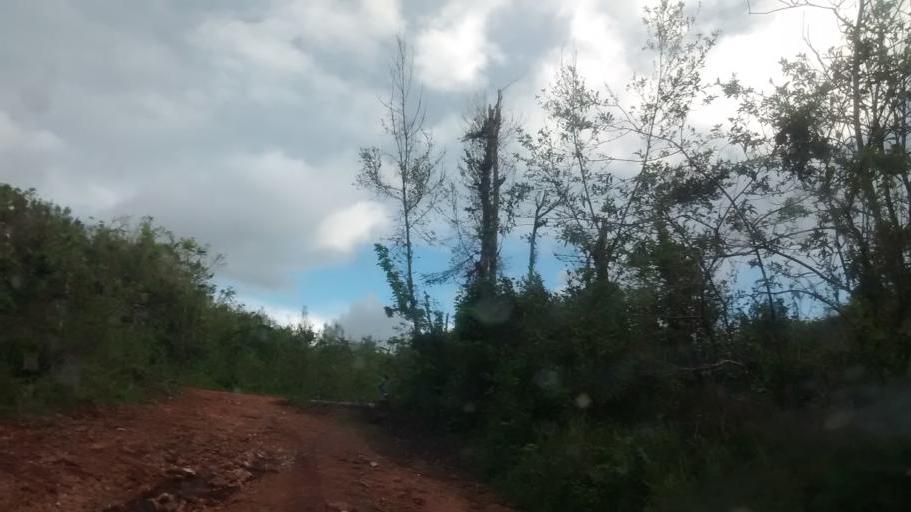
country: HT
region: Grandans
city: Corail
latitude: 18.5076
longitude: -73.7818
